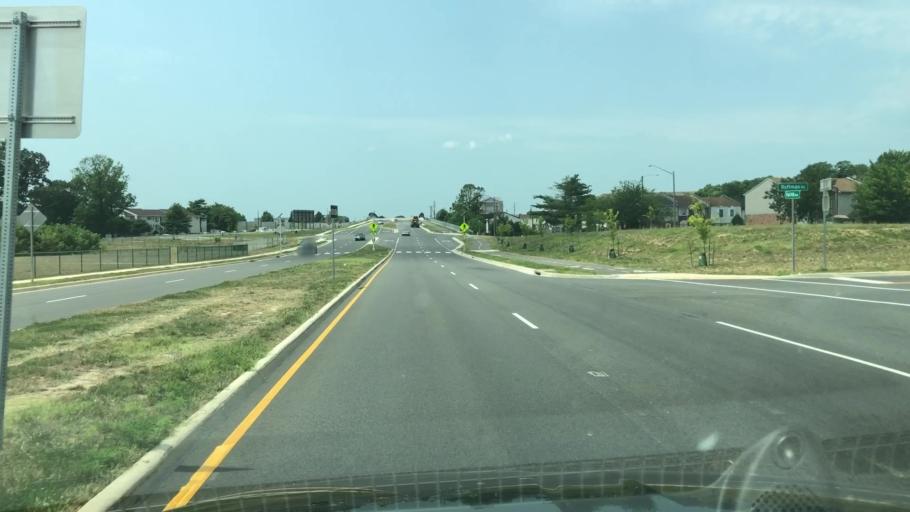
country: US
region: Virginia
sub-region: Stafford County
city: Falmouth
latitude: 38.3154
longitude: -77.4991
